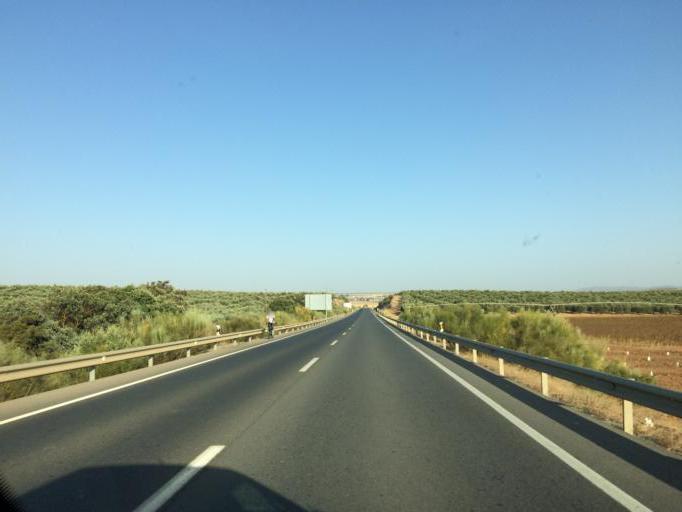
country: ES
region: Andalusia
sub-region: Provincia de Malaga
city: Humilladero
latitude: 37.0585
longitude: -4.6836
